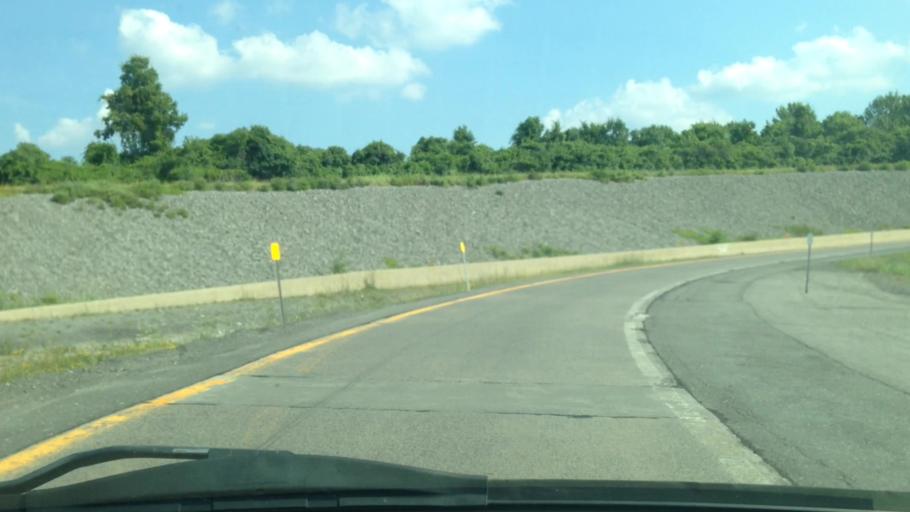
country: US
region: New York
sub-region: Onondaga County
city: Seneca Knolls
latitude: 43.1070
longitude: -76.2840
